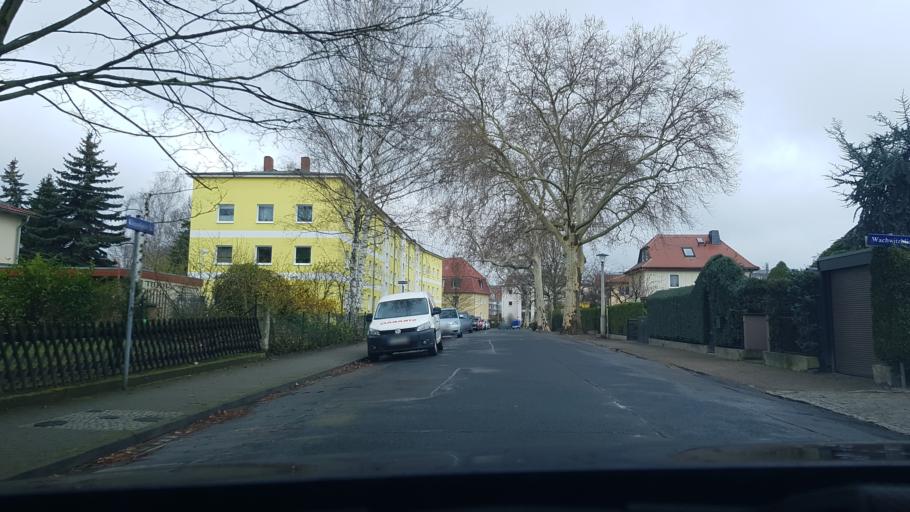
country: DE
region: Saxony
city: Heidenau
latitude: 51.0219
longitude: 13.8325
